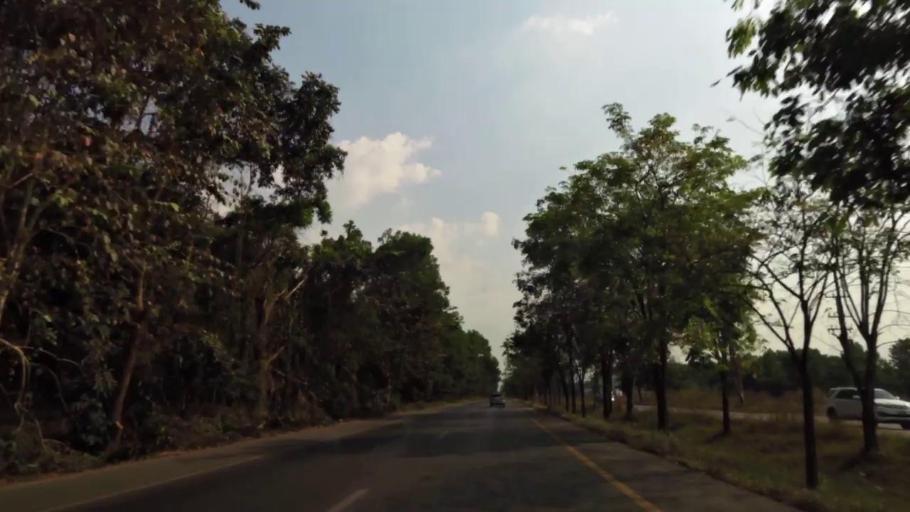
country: TH
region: Rayong
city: Wang Chan
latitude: 12.9089
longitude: 101.5363
